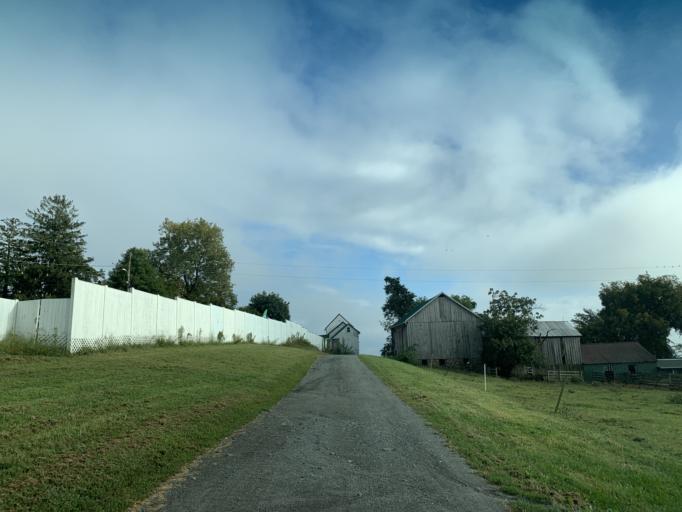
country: US
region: Maryland
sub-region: Harford County
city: Havre de Grace
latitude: 39.5625
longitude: -76.1286
